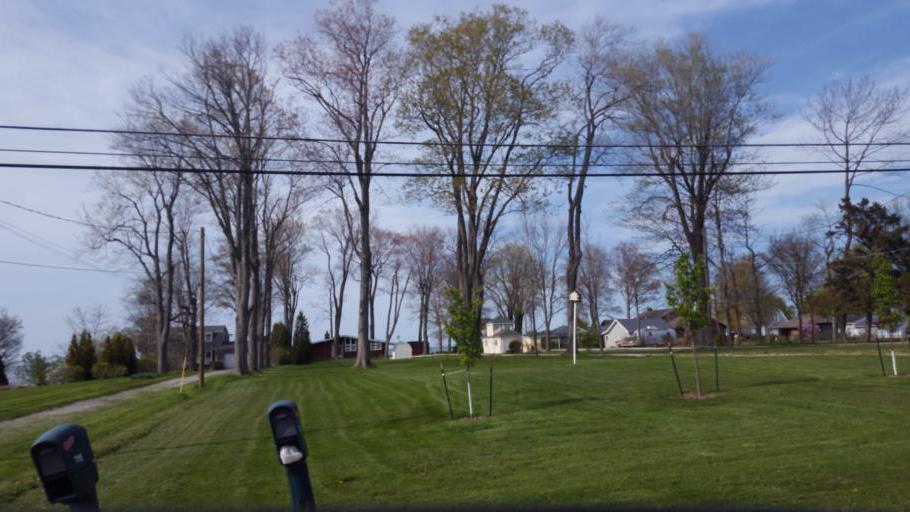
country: US
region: Ohio
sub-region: Lake County
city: North Madison
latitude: 41.8415
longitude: -81.0291
